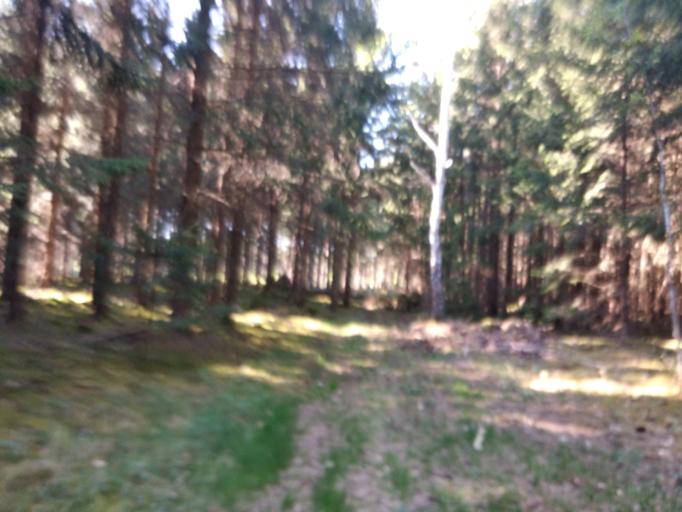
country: DE
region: Bavaria
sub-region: Upper Bavaria
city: Grasbrunn
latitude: 48.0921
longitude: 11.7488
